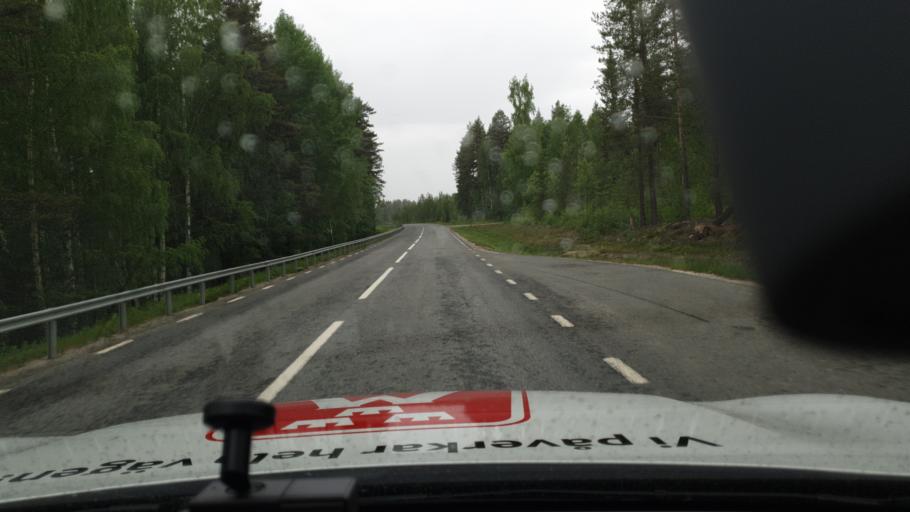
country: SE
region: Vaesterbotten
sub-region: Lycksele Kommun
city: Lycksele
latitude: 64.4391
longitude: 18.9519
